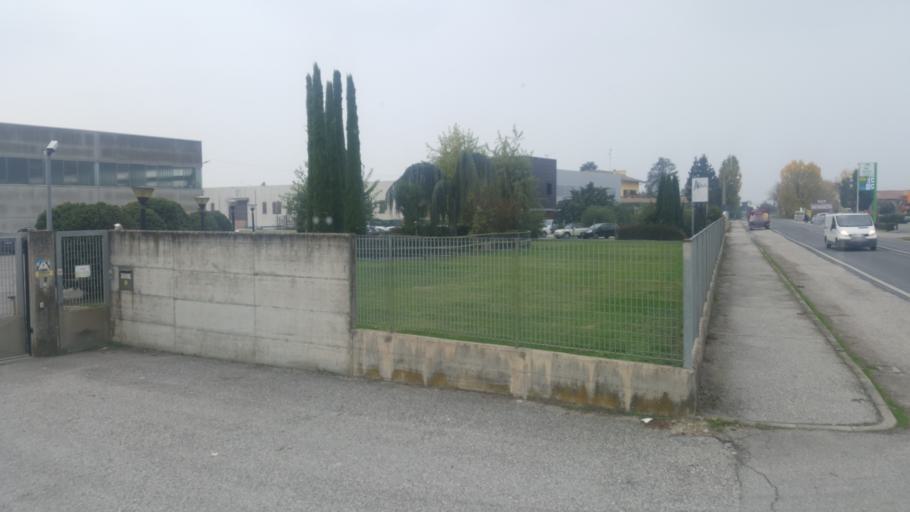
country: IT
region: Emilia-Romagna
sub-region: Provincia di Ferrara
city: Bondeno
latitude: 44.8995
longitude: 11.4050
